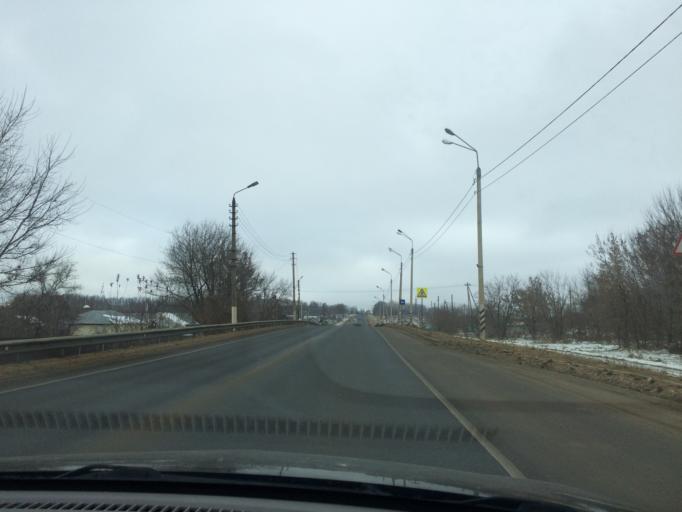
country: RU
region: Tula
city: Plavsk
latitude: 53.7164
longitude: 37.2975
